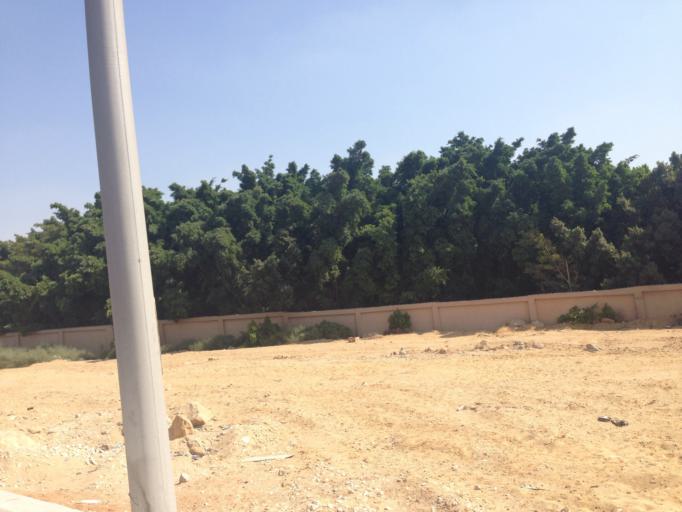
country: EG
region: Muhafazat al Qalyubiyah
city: Al Khankah
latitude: 30.0696
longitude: 31.4279
